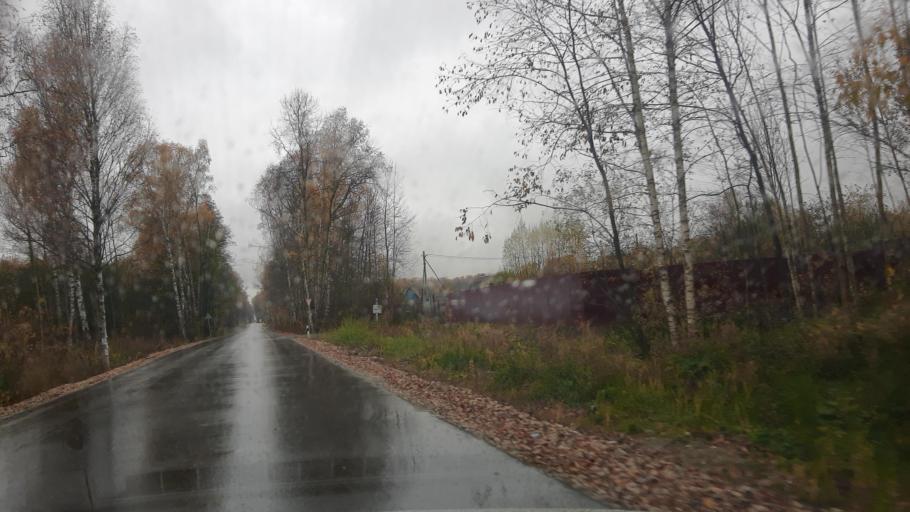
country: RU
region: Moskovskaya
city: Elektrostal'
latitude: 55.7981
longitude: 38.3727
